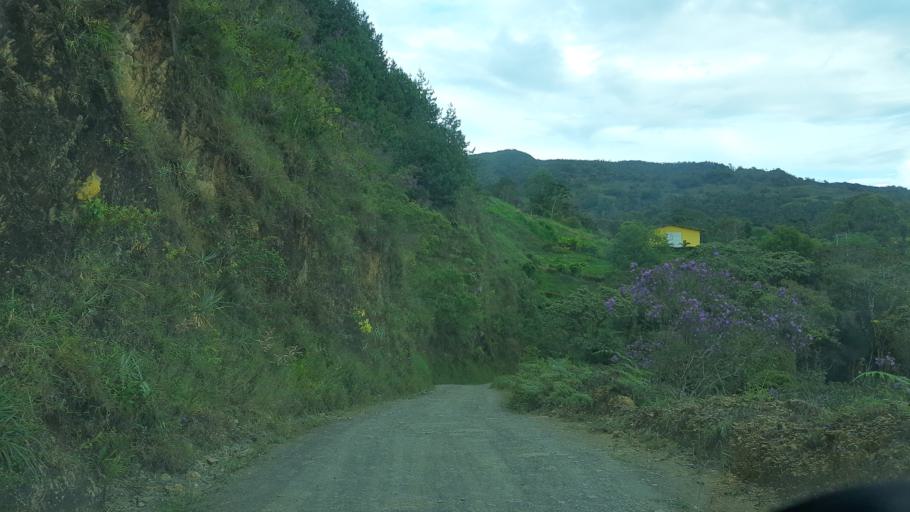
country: CO
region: Boyaca
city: Garagoa
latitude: 4.9994
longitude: -73.3312
